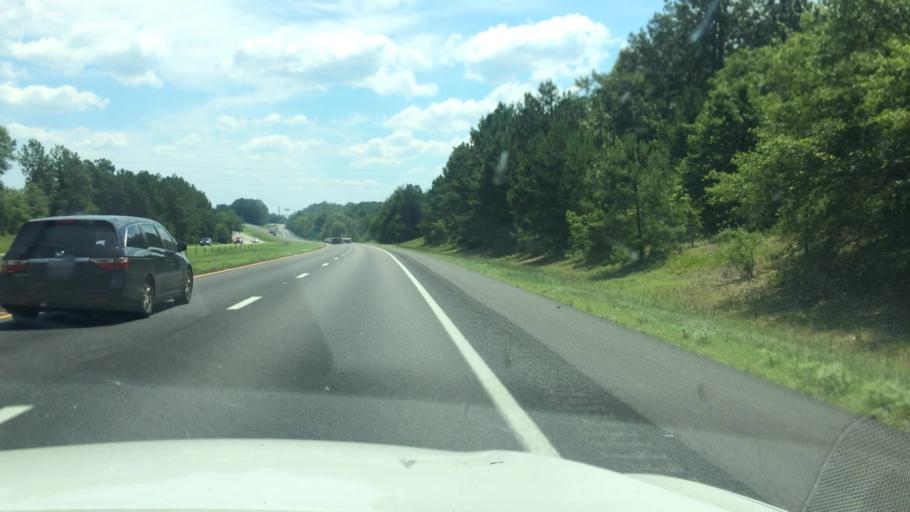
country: US
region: South Carolina
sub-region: Aiken County
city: Aiken
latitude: 33.6362
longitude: -81.7520
